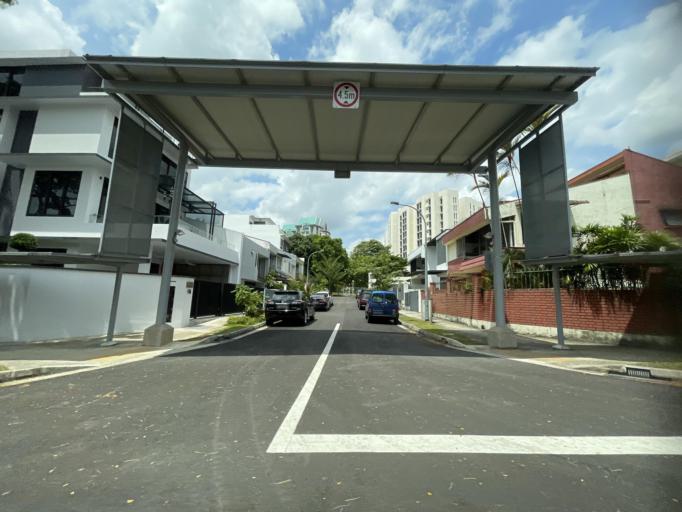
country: MY
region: Johor
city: Johor Bahru
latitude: 1.3717
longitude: 103.7674
